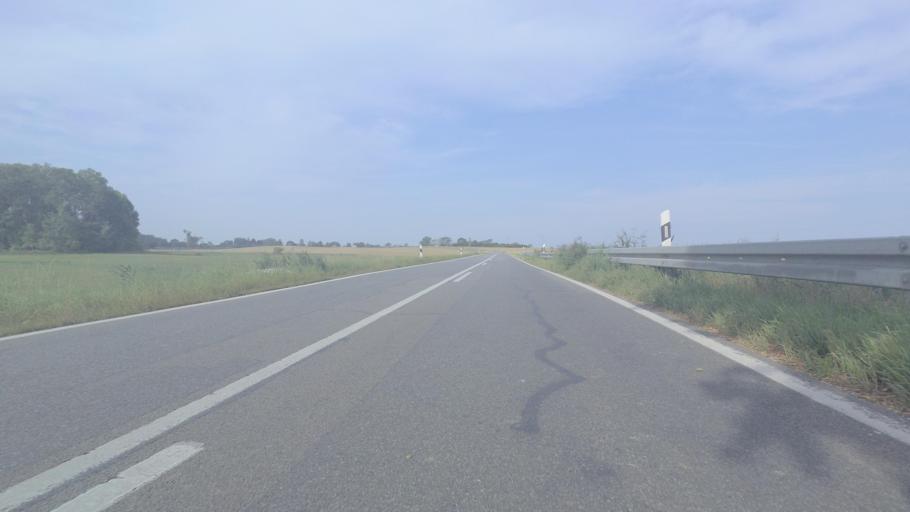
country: DE
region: Mecklenburg-Vorpommern
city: Wackerow
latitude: 53.6545
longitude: 12.8767
